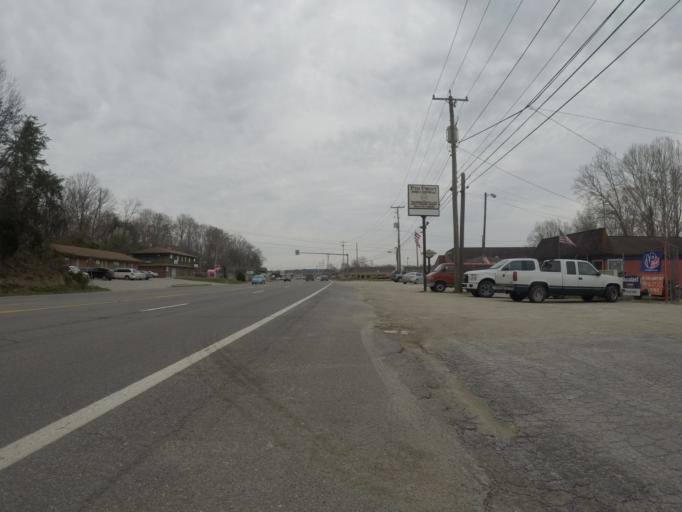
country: US
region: West Virginia
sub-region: Cabell County
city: Pea Ridge
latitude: 38.4125
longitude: -82.3124
